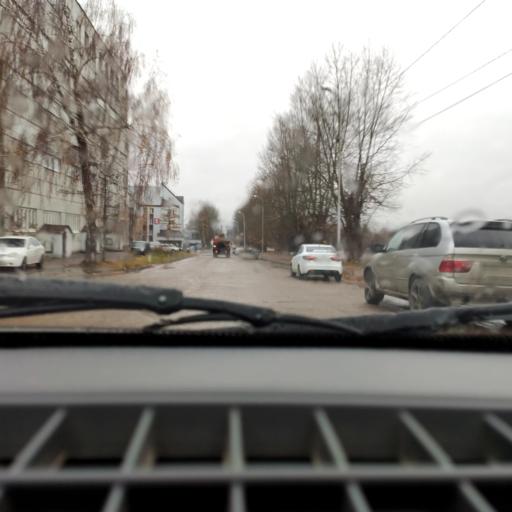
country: RU
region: Bashkortostan
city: Ufa
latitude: 54.8093
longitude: 56.0785
